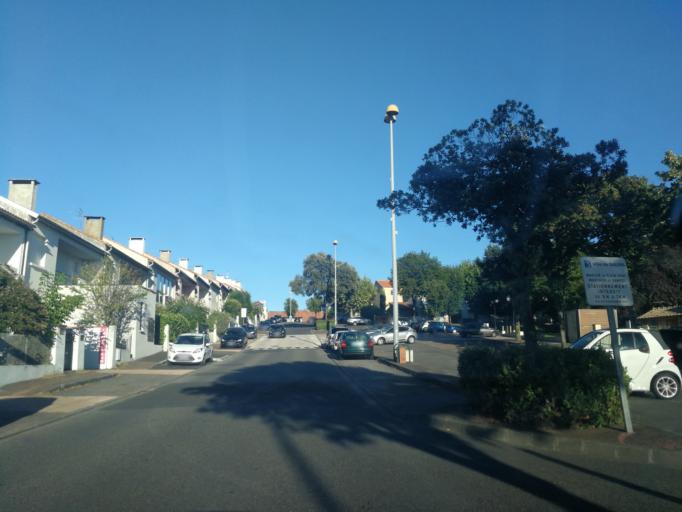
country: FR
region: Midi-Pyrenees
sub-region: Departement de la Haute-Garonne
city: Balma
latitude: 43.6092
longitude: 1.4953
